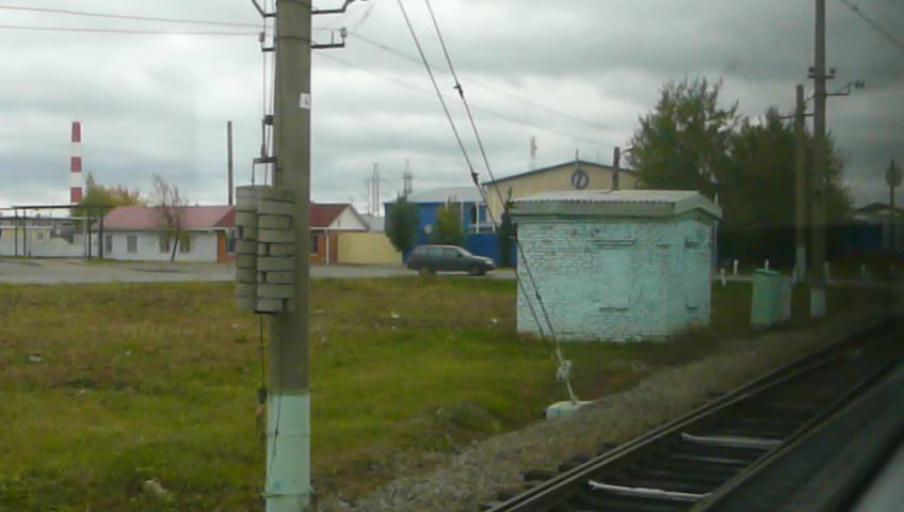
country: RU
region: Moskovskaya
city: Yegor'yevsk
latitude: 55.3936
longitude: 39.0062
